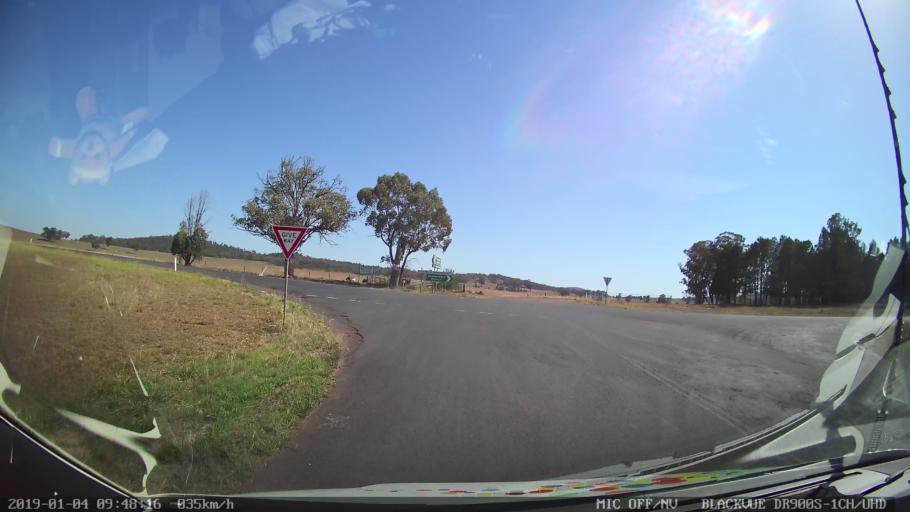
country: AU
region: New South Wales
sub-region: Cabonne
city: Canowindra
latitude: -33.5984
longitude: 148.4325
